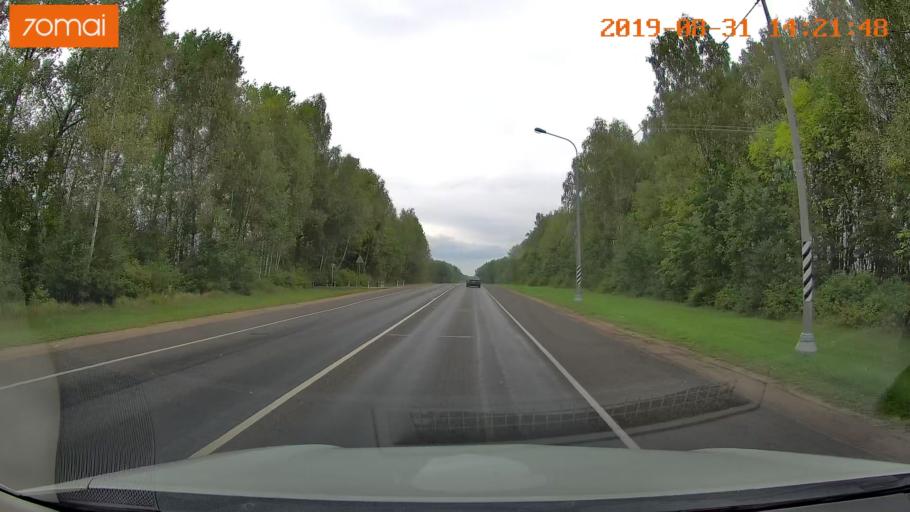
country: RU
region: Smolensk
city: Yekimovichi
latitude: 54.0875
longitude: 33.2042
